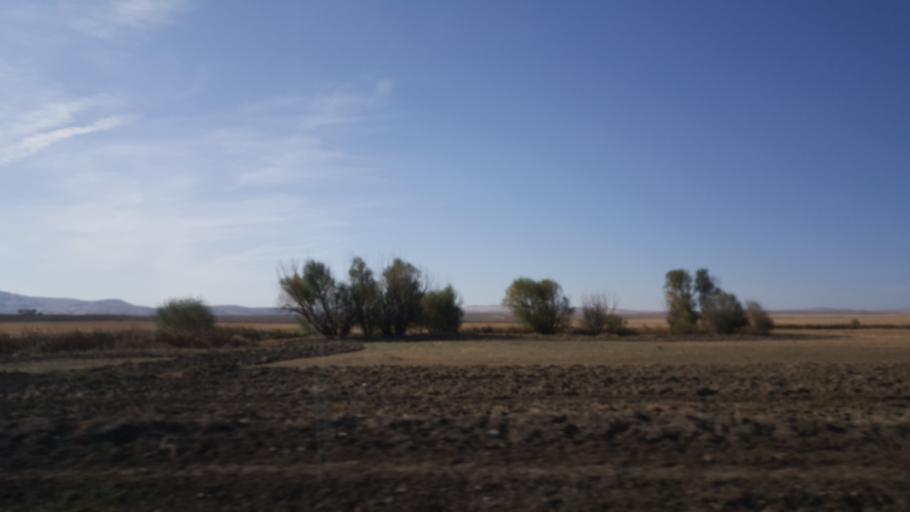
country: TR
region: Ankara
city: Yenice
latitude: 39.3684
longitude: 32.8107
